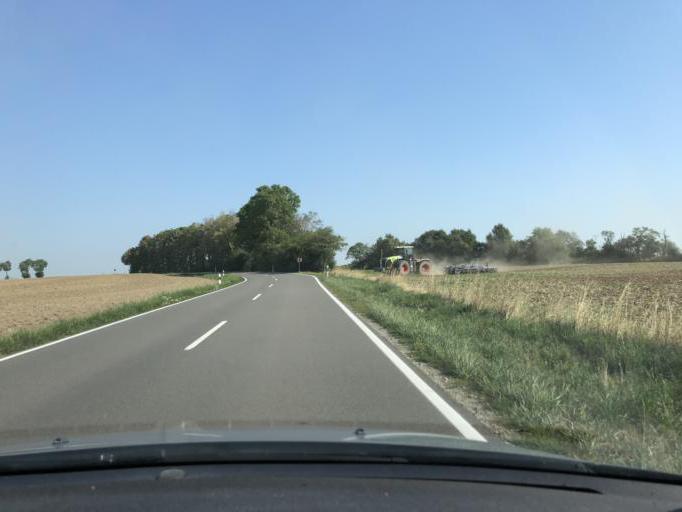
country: DE
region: Thuringia
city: Rastenberg
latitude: 51.1862
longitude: 11.4941
